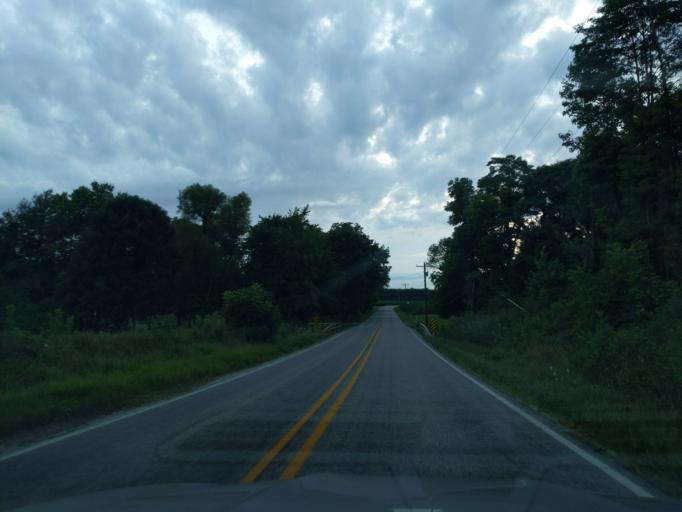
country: US
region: Indiana
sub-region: Ripley County
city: Osgood
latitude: 39.1984
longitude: -85.2986
